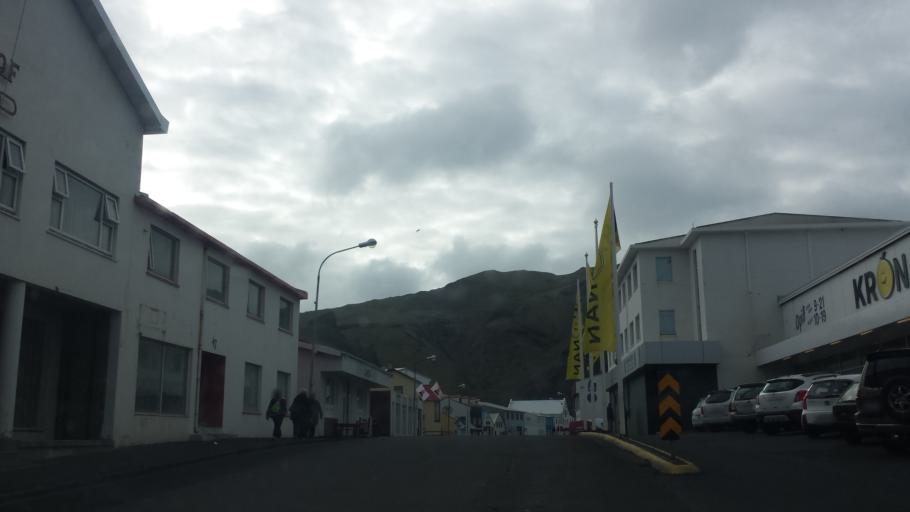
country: IS
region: South
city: Vestmannaeyjar
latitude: 63.4423
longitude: -20.2708
